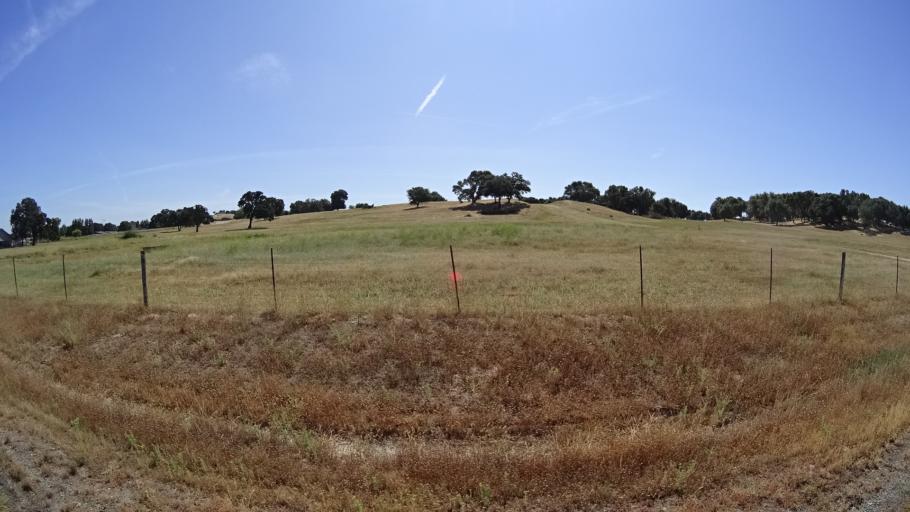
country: US
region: California
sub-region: Calaveras County
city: Rancho Calaveras
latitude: 38.1252
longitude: -120.9266
